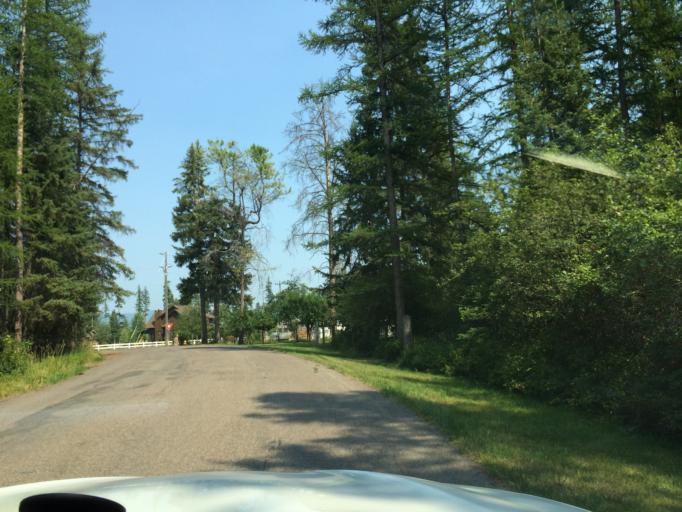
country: US
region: Montana
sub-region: Flathead County
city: Whitefish
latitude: 48.3994
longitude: -114.3283
